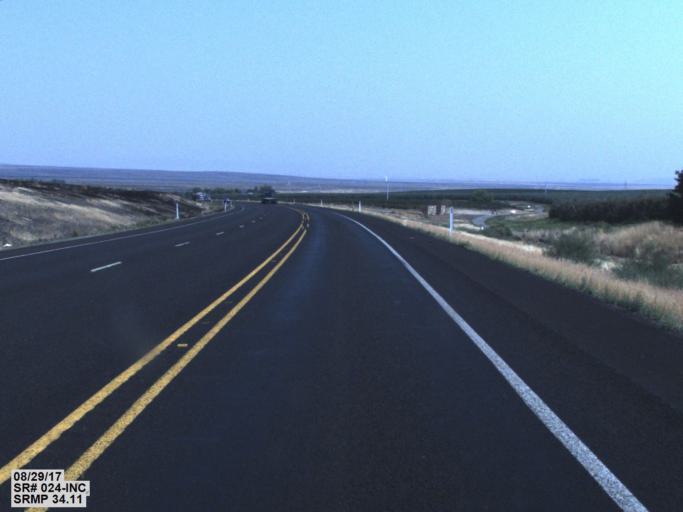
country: US
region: Washington
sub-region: Grant County
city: Desert Aire
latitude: 46.5568
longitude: -119.8121
